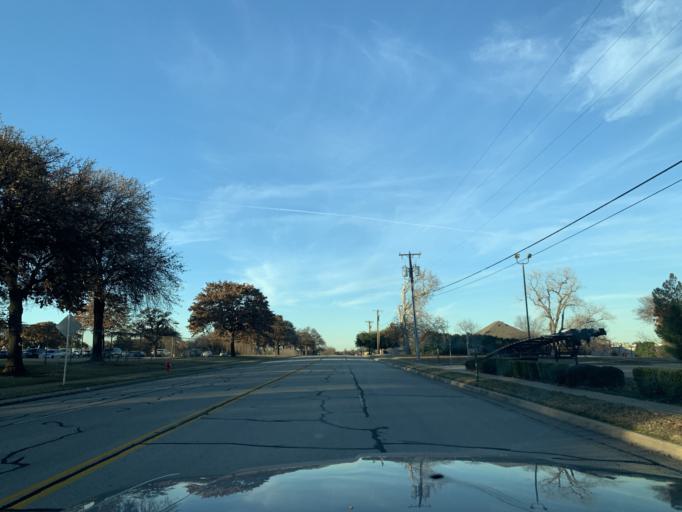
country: US
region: Texas
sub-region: Tarrant County
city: Bedford
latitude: 32.8389
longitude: -97.1373
